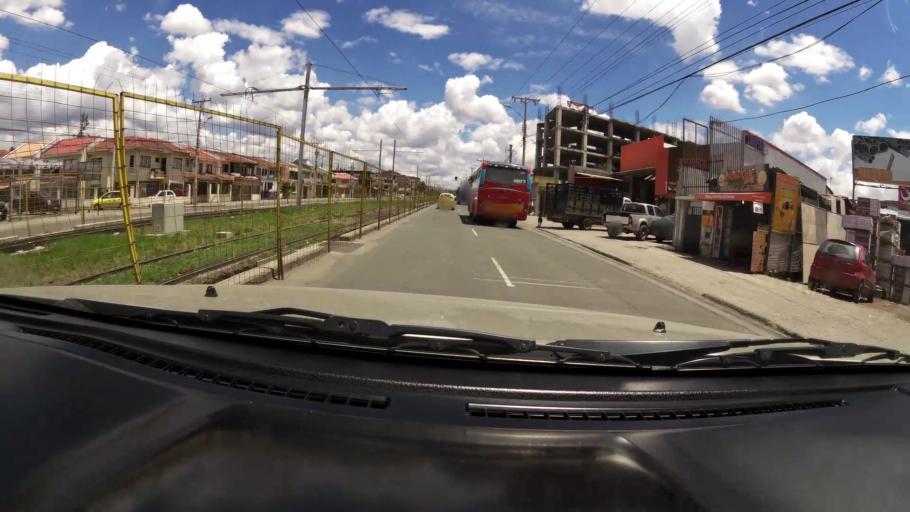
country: EC
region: Azuay
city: Cuenca
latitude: -2.9142
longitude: -79.0373
